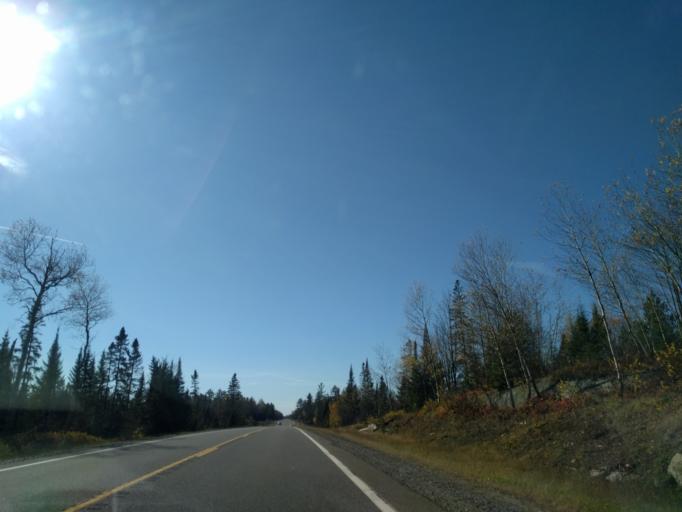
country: US
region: Michigan
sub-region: Marquette County
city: West Ishpeming
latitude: 46.4284
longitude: -87.9702
